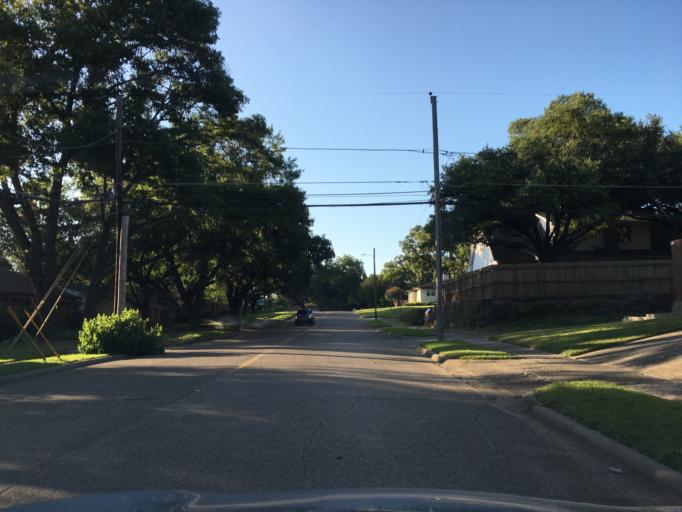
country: US
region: Texas
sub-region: Dallas County
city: Highland Park
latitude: 32.8607
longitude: -96.7363
